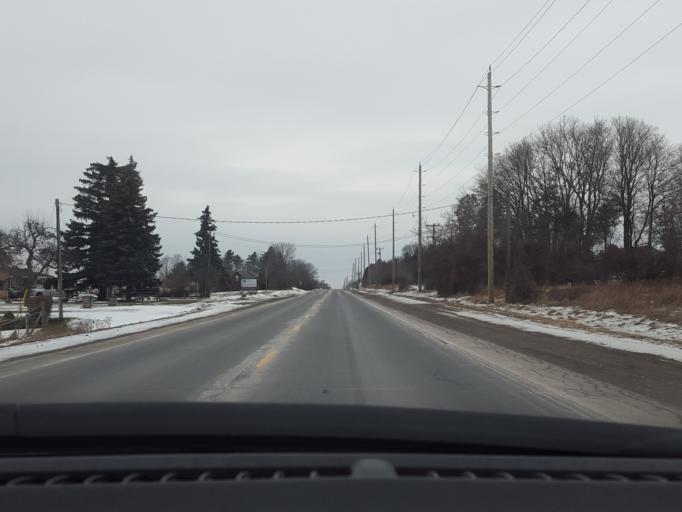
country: CA
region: Ontario
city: Keswick
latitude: 44.1651
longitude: -79.4313
